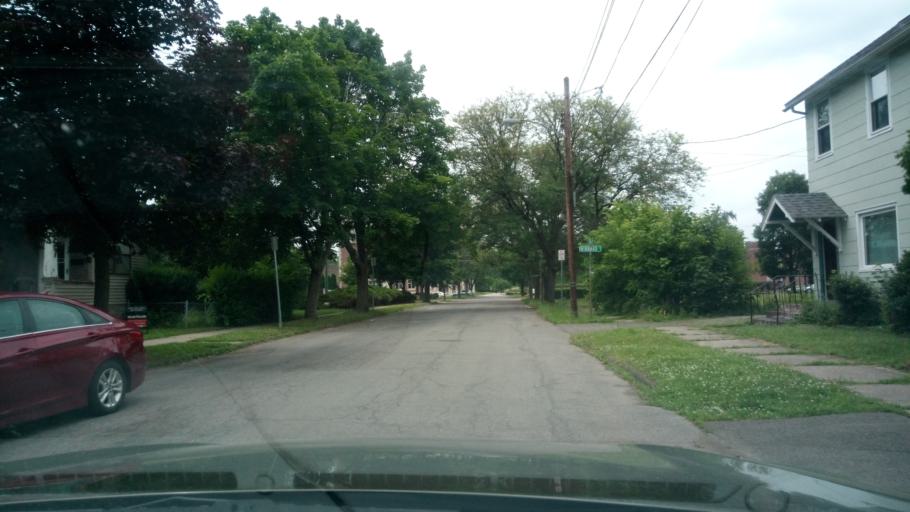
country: US
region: New York
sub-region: Chemung County
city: Elmira
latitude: 42.0940
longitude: -76.8146
